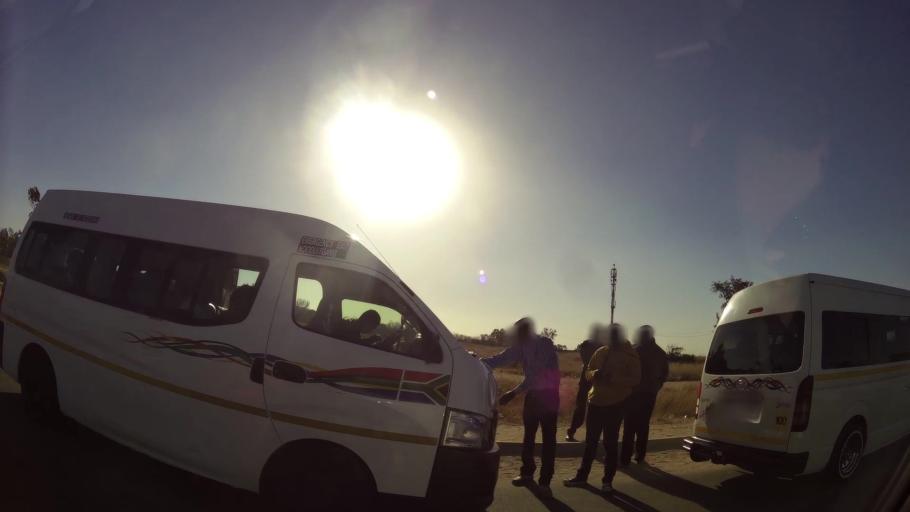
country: ZA
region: Gauteng
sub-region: City of Johannesburg Metropolitan Municipality
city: Diepsloot
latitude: -25.9368
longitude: 27.9897
